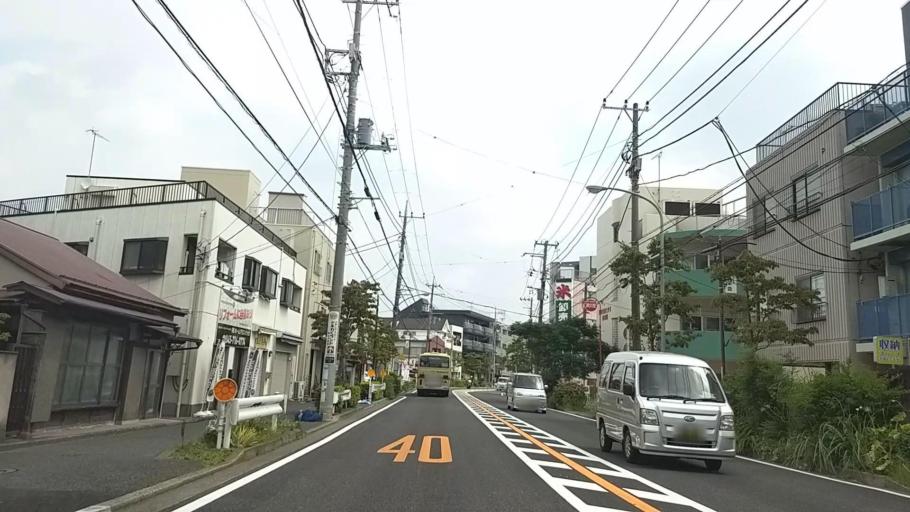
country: JP
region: Kanagawa
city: Yokohama
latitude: 35.4304
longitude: 139.5974
